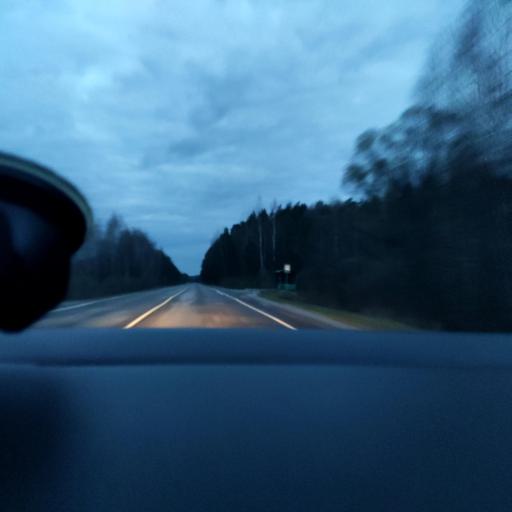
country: RU
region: Moskovskaya
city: Shaturtorf
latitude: 55.4288
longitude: 39.3460
